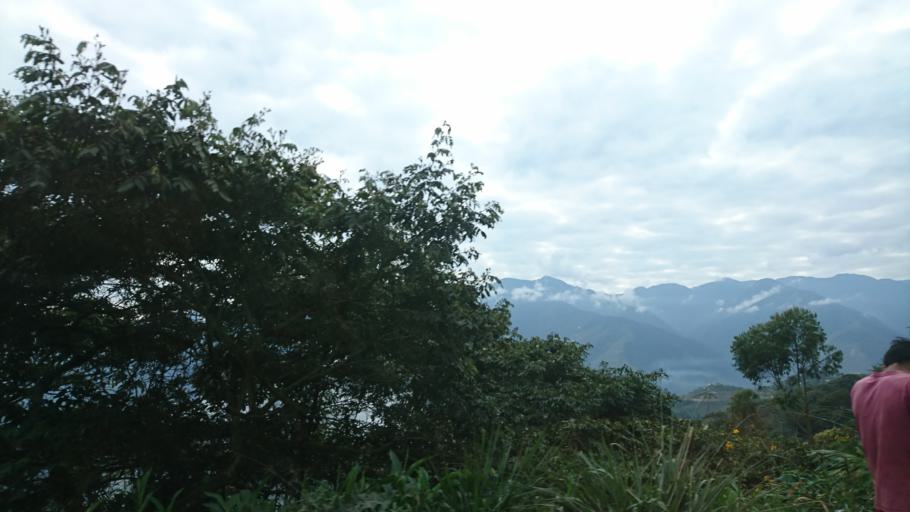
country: BO
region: La Paz
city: Coroico
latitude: -16.1904
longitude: -67.7226
